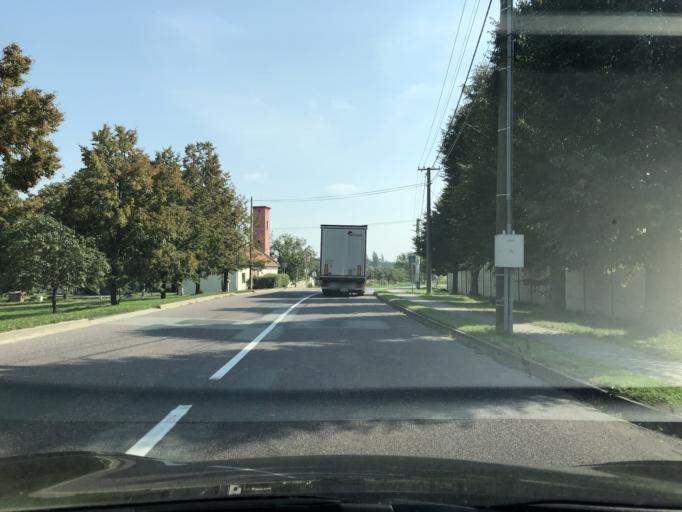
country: CZ
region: South Moravian
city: Brezi
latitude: 48.8262
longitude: 16.5374
